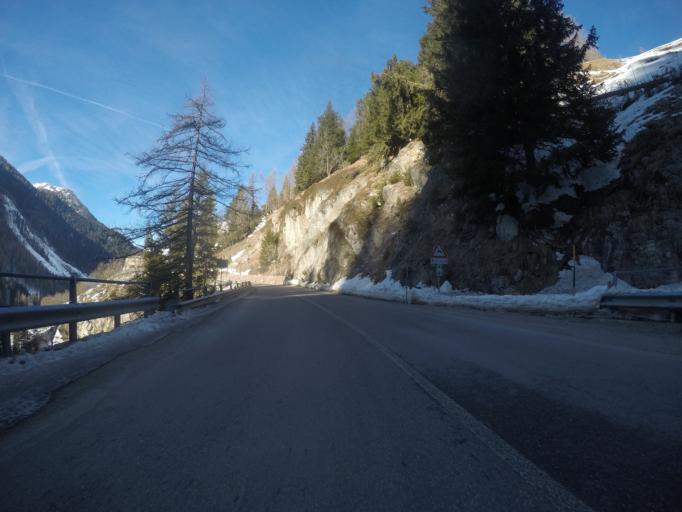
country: IT
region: Veneto
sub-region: Provincia di Belluno
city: Livinallongo del Col di Lana
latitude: 46.4976
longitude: 11.9199
